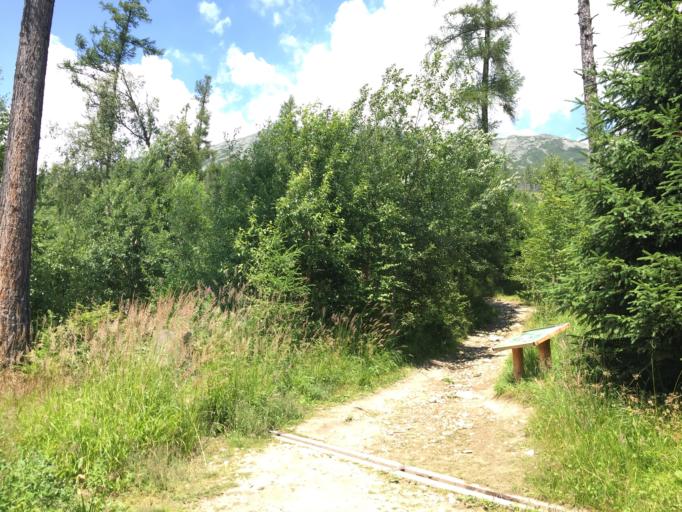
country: SK
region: Presovsky
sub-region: Okres Poprad
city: Vysoke Tatry
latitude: 49.1486
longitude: 20.2144
